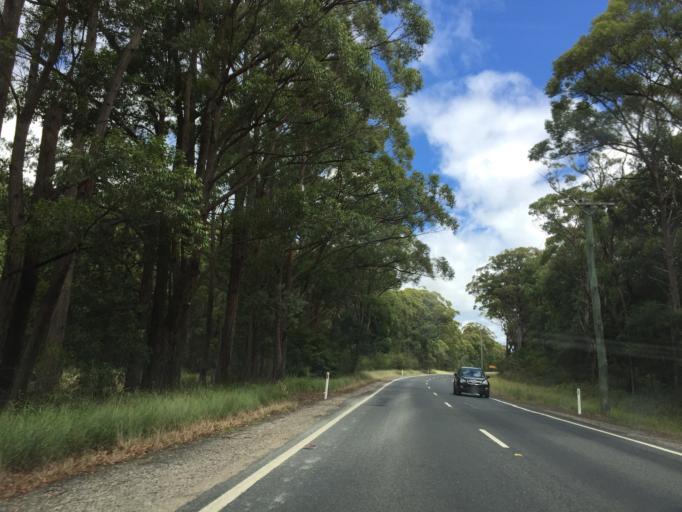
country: AU
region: New South Wales
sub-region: Hawkesbury
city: Richmond
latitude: -33.5167
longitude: 150.5934
